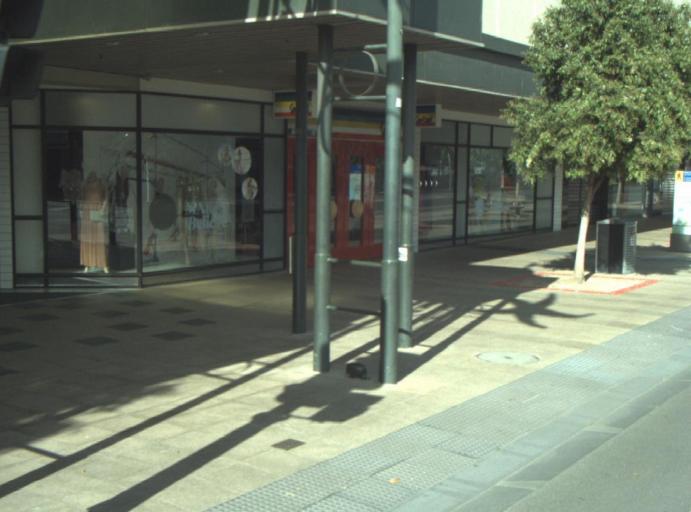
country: AU
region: Victoria
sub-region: Greater Geelong
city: Geelong
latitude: -38.1477
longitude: 144.3623
